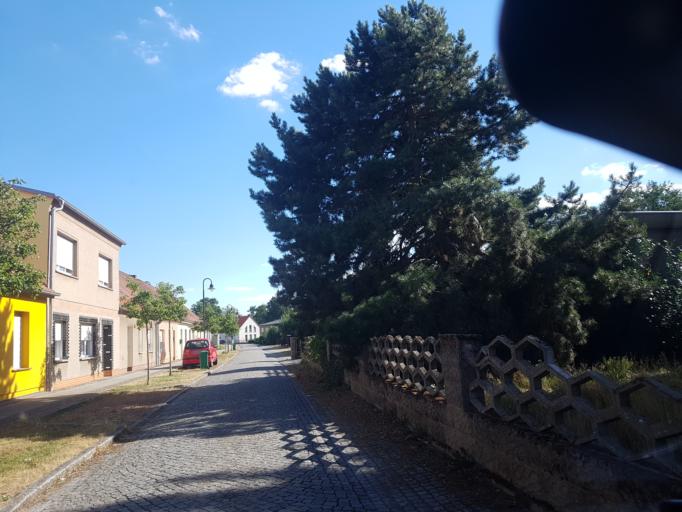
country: DE
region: Brandenburg
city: Juterbog
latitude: 52.0224
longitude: 13.1014
